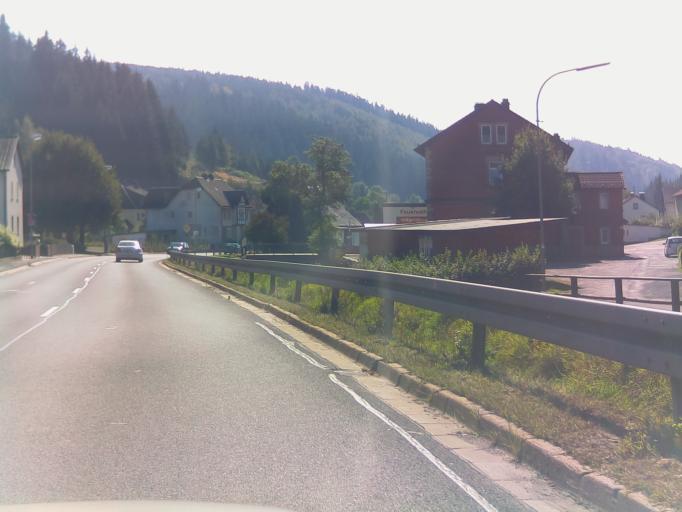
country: DE
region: Bavaria
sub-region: Upper Franconia
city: Teuschnitz
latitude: 50.3901
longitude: 11.3480
